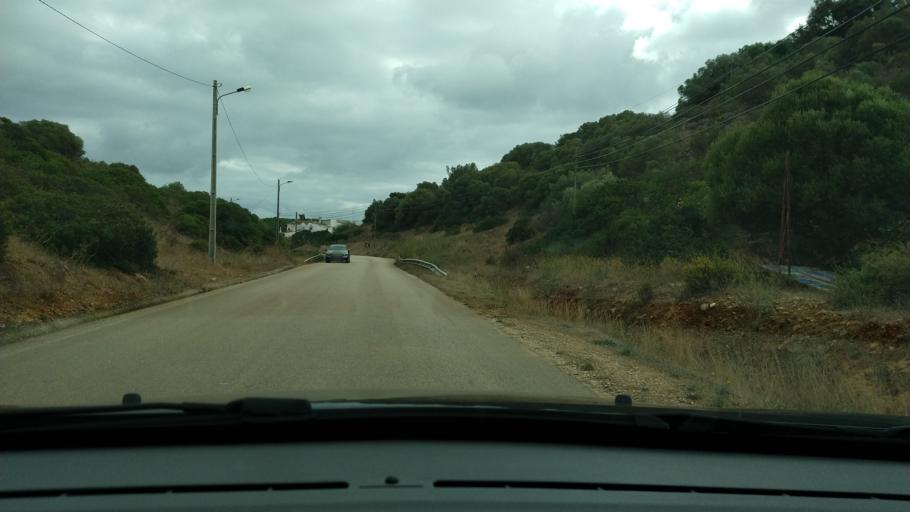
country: PT
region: Faro
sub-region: Lagos
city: Lagos
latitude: 37.0815
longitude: -8.7773
